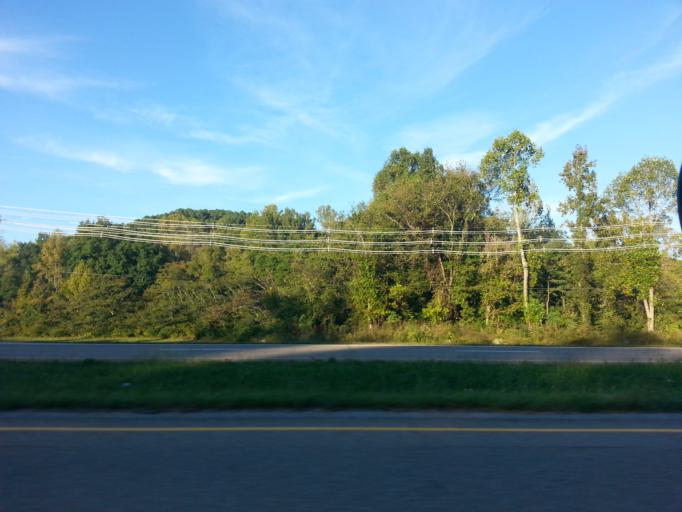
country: US
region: Tennessee
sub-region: Blount County
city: Wildwood
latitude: 35.7489
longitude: -83.8386
